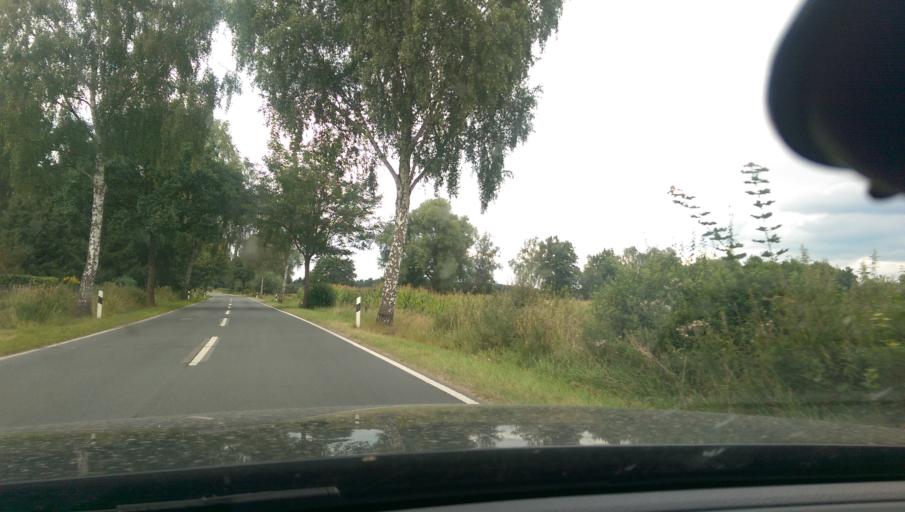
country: DE
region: Lower Saxony
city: Elze
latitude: 52.5771
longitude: 9.7136
